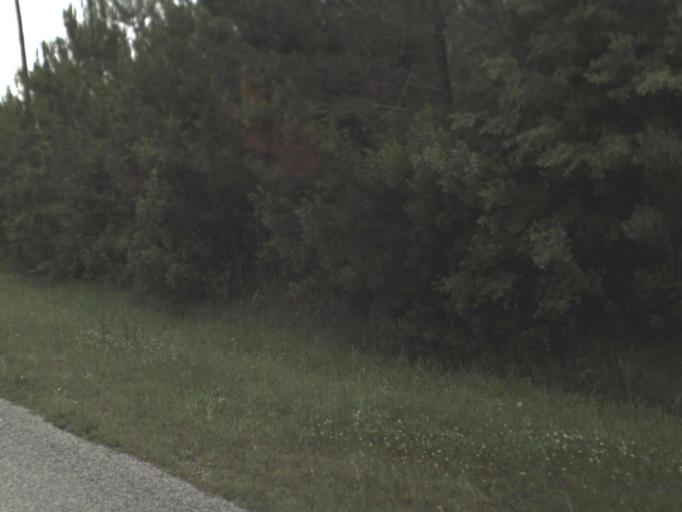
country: US
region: Florida
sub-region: Duval County
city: Jacksonville
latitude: 30.4672
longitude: -81.6722
